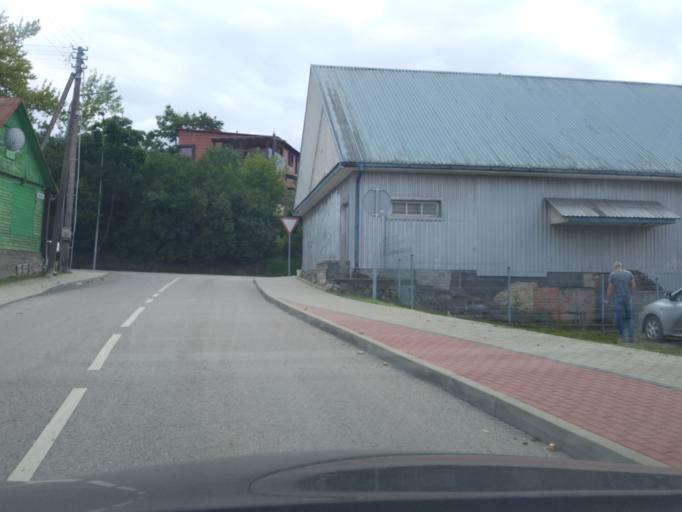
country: LT
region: Alytaus apskritis
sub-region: Alytus
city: Alytus
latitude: 54.4015
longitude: 24.0472
